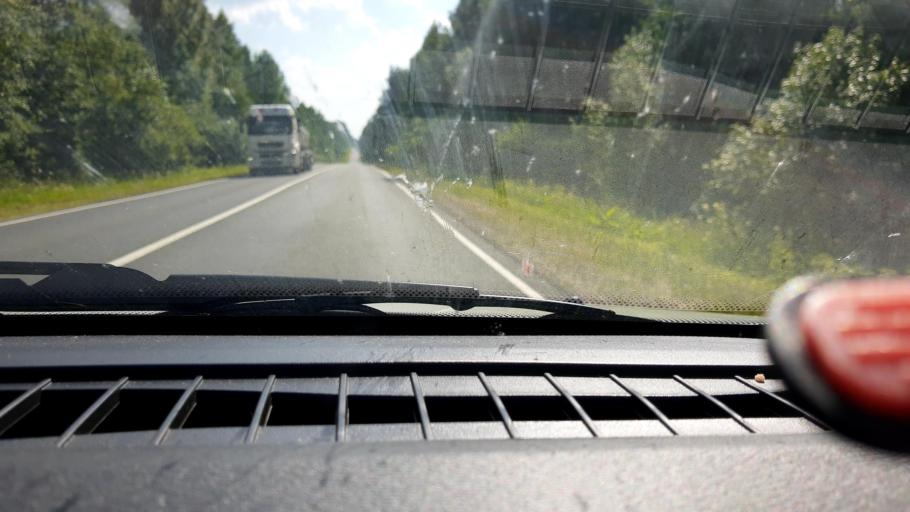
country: RU
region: Nizjnij Novgorod
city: Uren'
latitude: 57.2710
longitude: 45.6268
